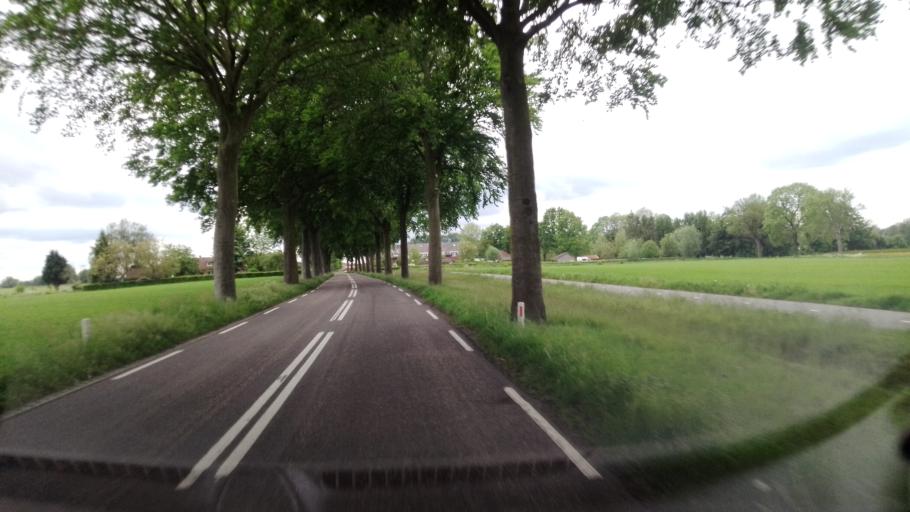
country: NL
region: Limburg
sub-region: Gemeente Venlo
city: Arcen
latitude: 51.4451
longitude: 6.1502
